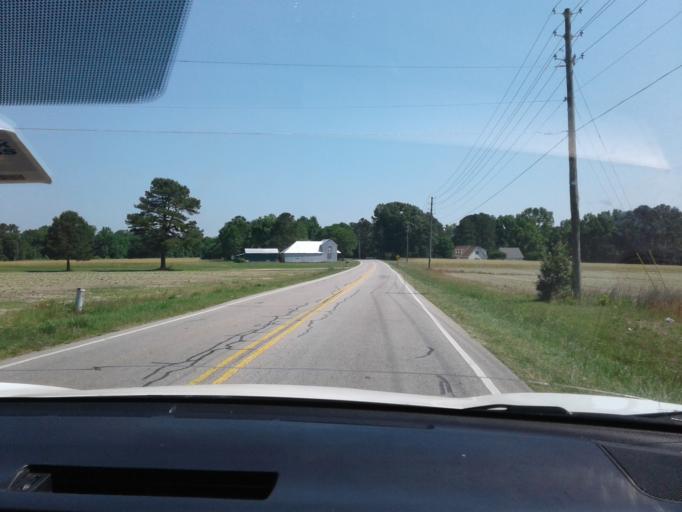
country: US
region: North Carolina
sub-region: Wake County
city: Fuquay-Varina
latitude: 35.5876
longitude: -78.8394
